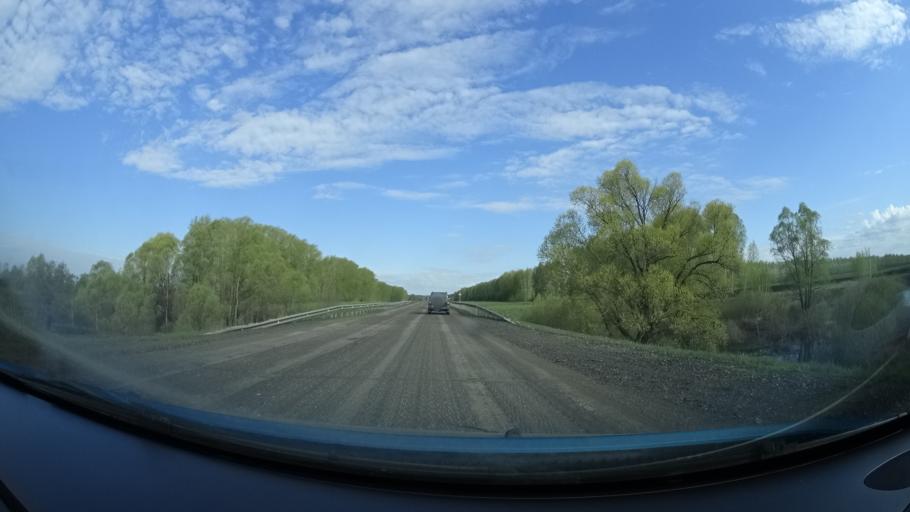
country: RU
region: Bashkortostan
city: Birsk
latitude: 55.2459
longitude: 55.7620
